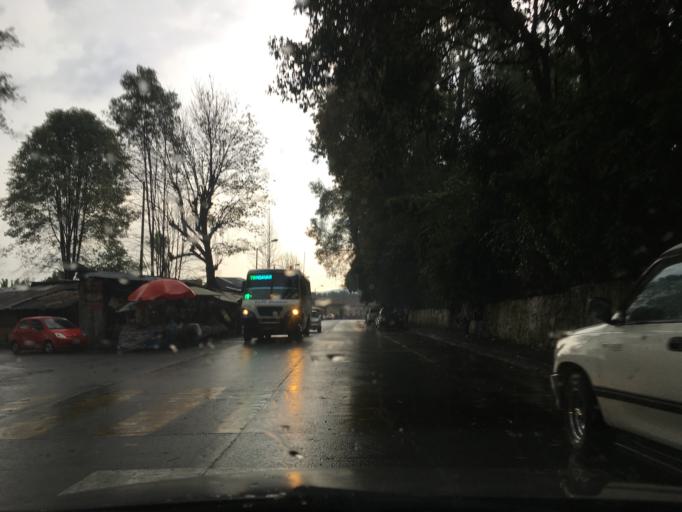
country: MX
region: Michoacan
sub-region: Uruapan
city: Uruapan
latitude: 19.4256
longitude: -102.0716
